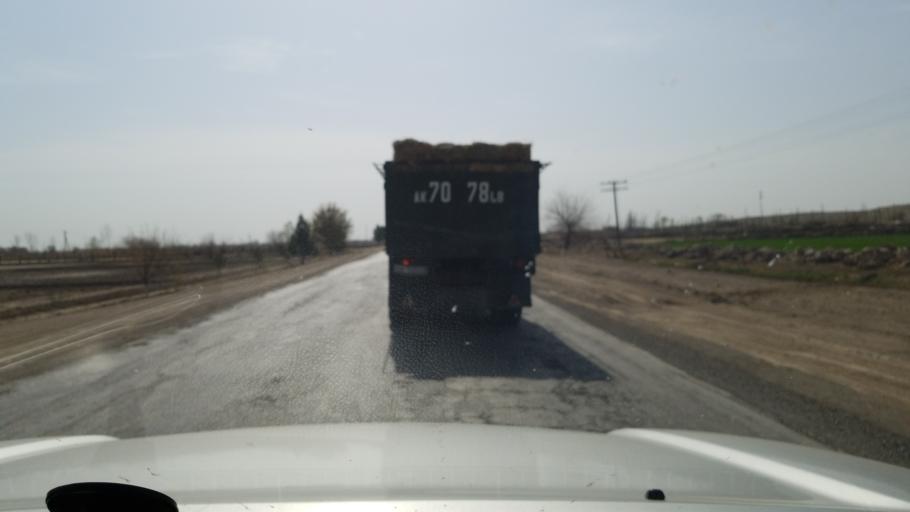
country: TM
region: Lebap
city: Sayat
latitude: 38.8600
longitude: 63.7991
